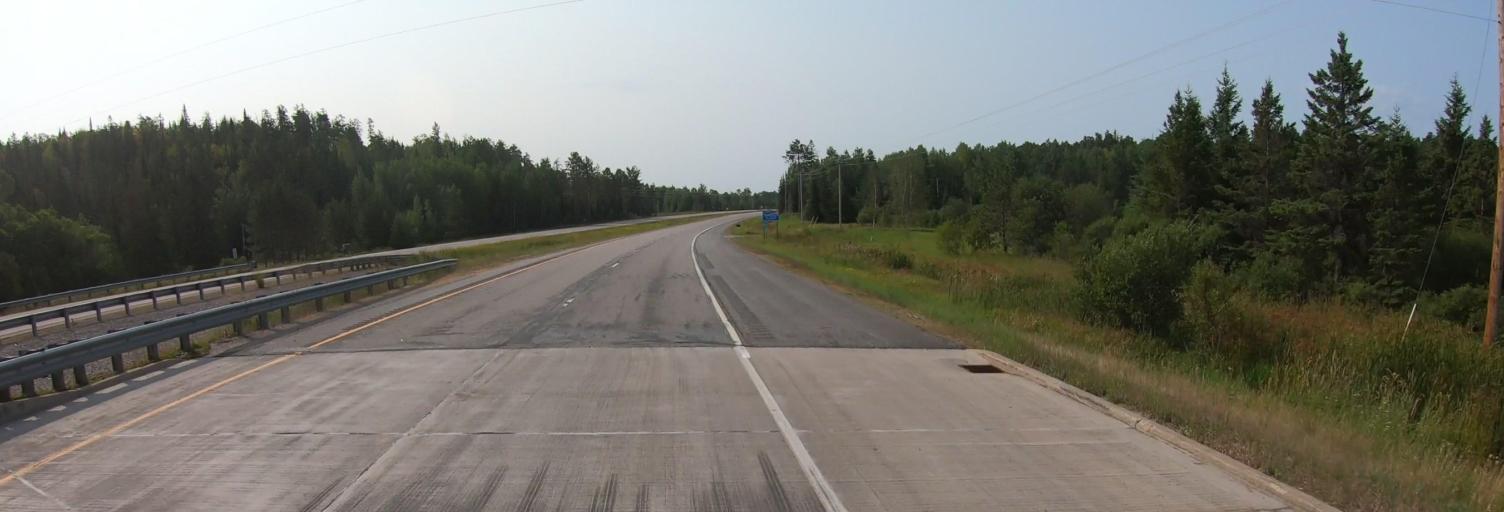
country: US
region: Minnesota
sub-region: Saint Louis County
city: Mountain Iron
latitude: 47.7075
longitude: -92.6426
